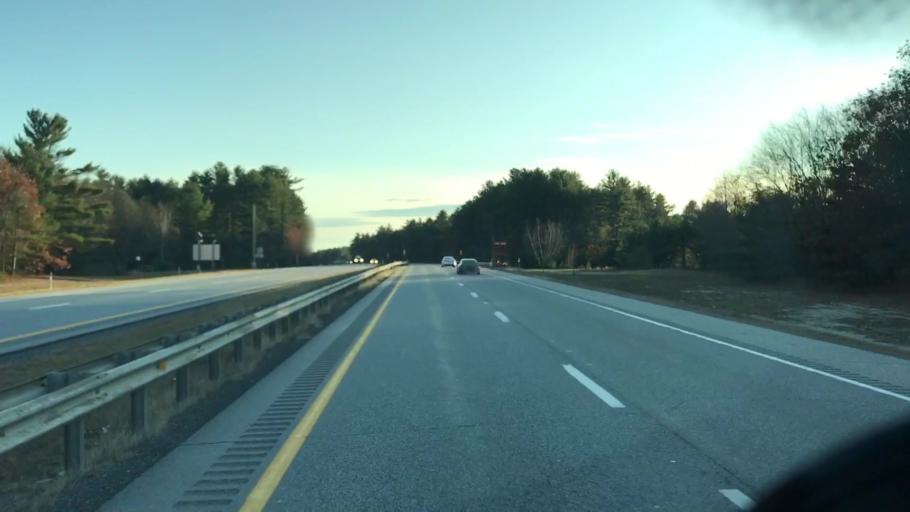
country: US
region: Maine
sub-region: Cumberland County
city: New Gloucester
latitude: 43.9991
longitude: -70.3080
